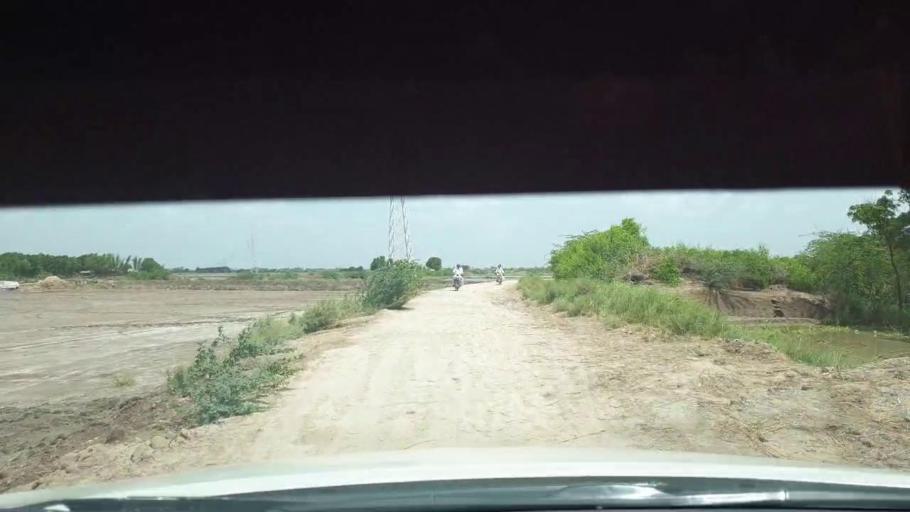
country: PK
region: Sindh
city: Kadhan
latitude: 24.4919
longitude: 68.9820
